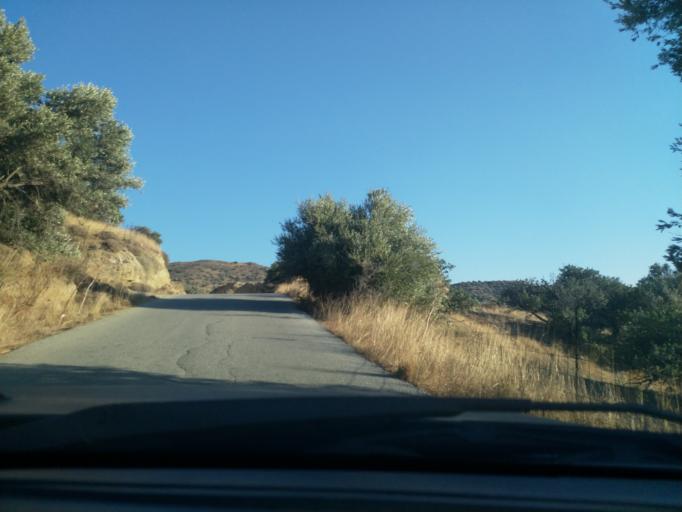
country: GR
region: Crete
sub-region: Nomos Rethymnis
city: Agia Galini
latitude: 35.1185
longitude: 24.5614
